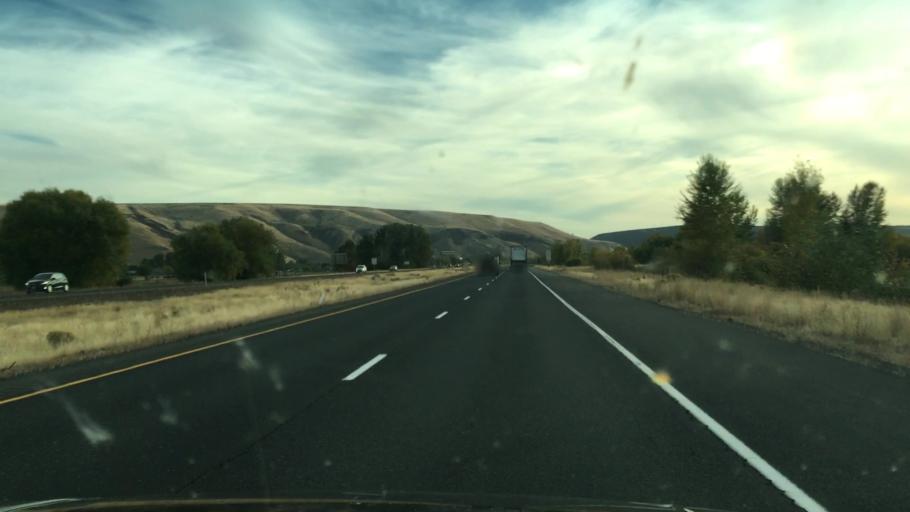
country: US
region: Washington
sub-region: Yakima County
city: Selah
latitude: 46.6697
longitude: -120.4886
